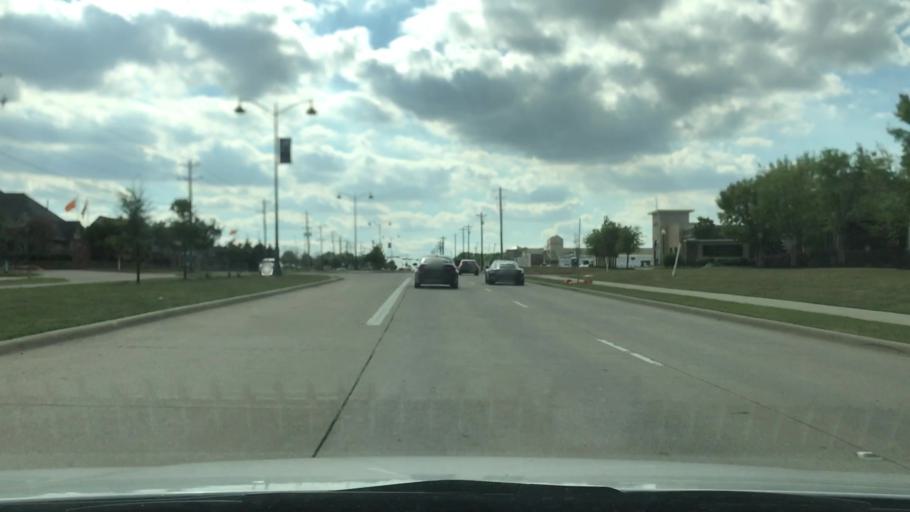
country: US
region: Texas
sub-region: Collin County
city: Allen
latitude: 33.1522
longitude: -96.7284
